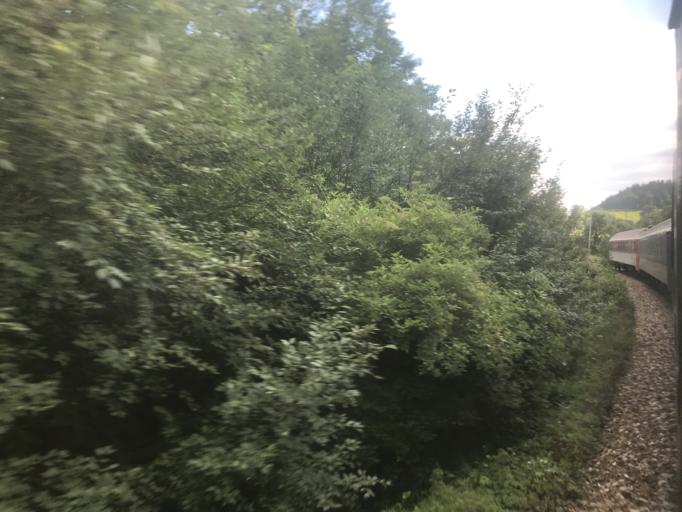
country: CZ
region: Jihocesky
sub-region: Okres Cesky Krumlov
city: Kaplice
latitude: 48.7346
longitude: 14.4501
